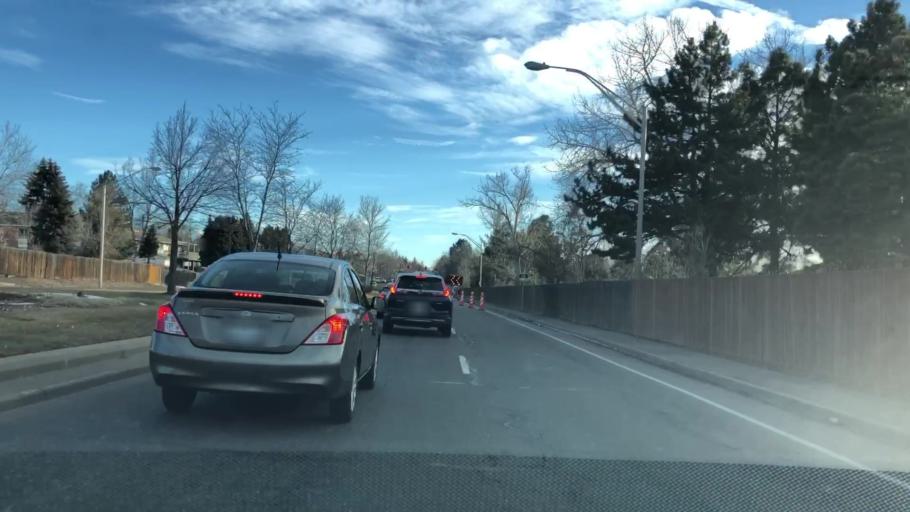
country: US
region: Colorado
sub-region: Adams County
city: Aurora
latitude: 39.6558
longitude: -104.7914
